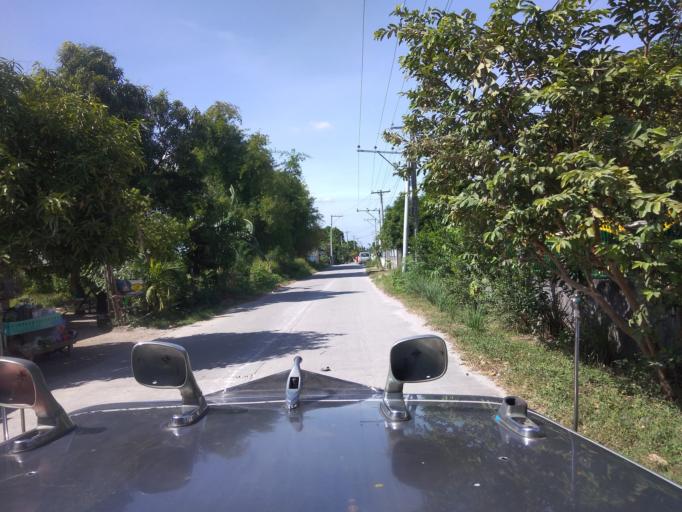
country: PH
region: Central Luzon
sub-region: Province of Pampanga
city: Magliman
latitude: 15.0226
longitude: 120.6543
